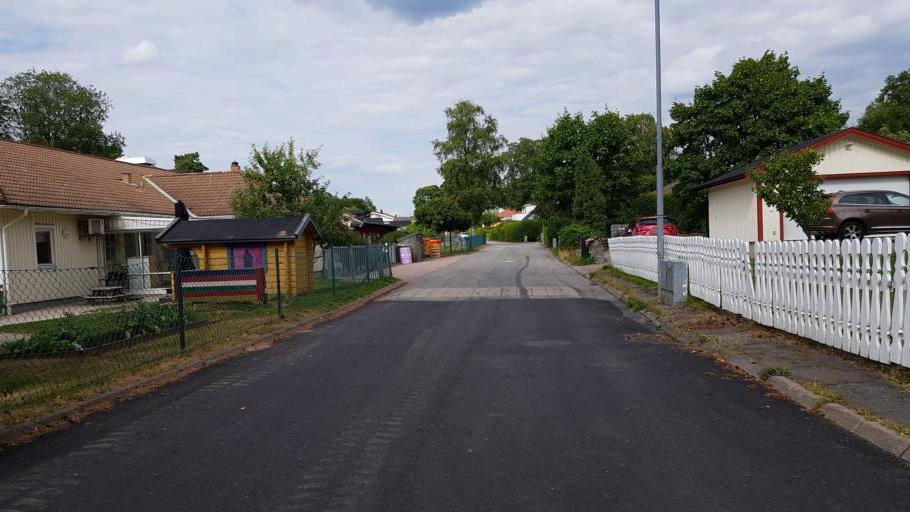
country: SE
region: Vaestra Goetaland
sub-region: Partille Kommun
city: Furulund
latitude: 57.7072
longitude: 12.1421
